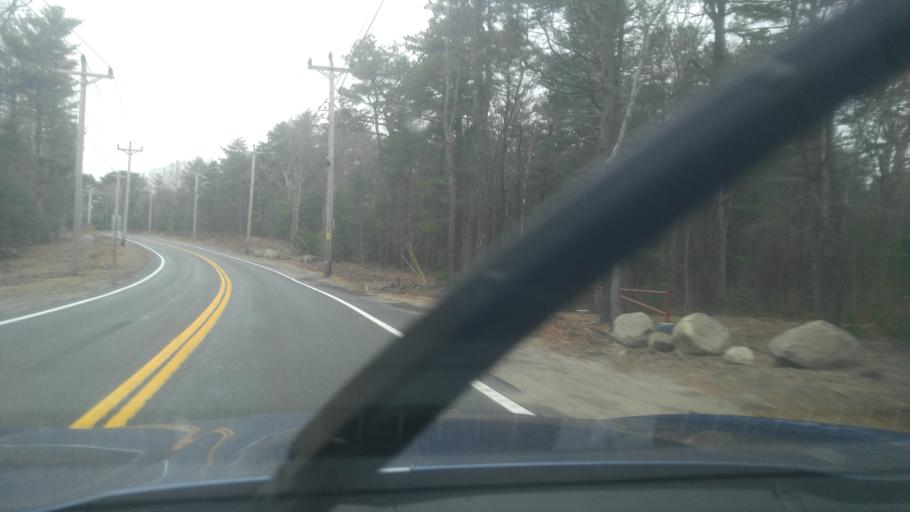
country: US
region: Rhode Island
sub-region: Kent County
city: West Warwick
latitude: 41.6545
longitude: -71.5582
